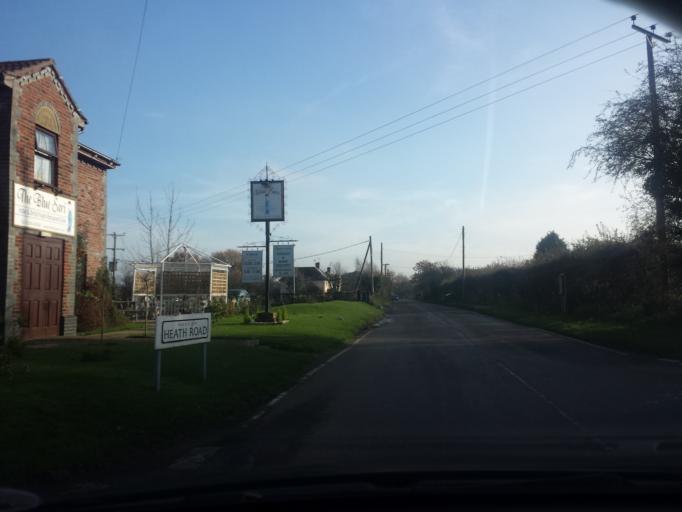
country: GB
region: England
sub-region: Essex
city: Saint Osyth
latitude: 51.8241
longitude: 1.1017
